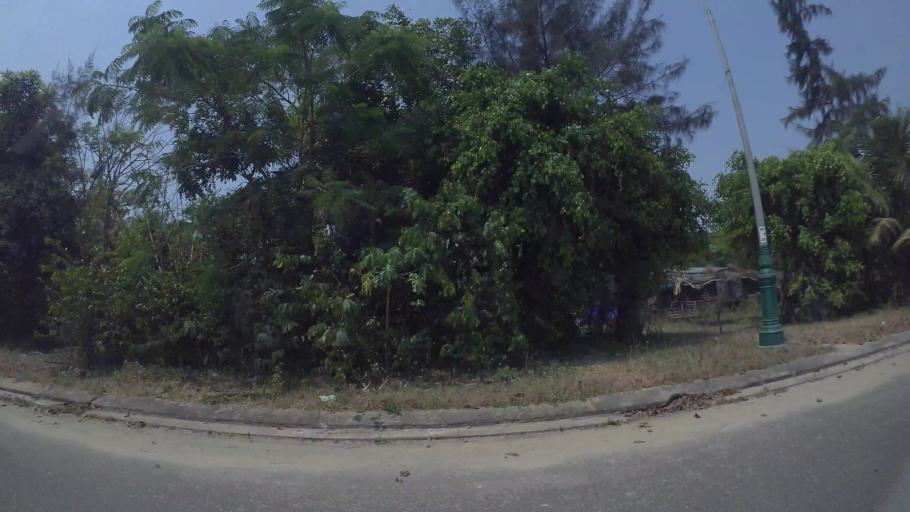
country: VN
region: Da Nang
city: Ngu Hanh Son
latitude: 15.9891
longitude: 108.2582
